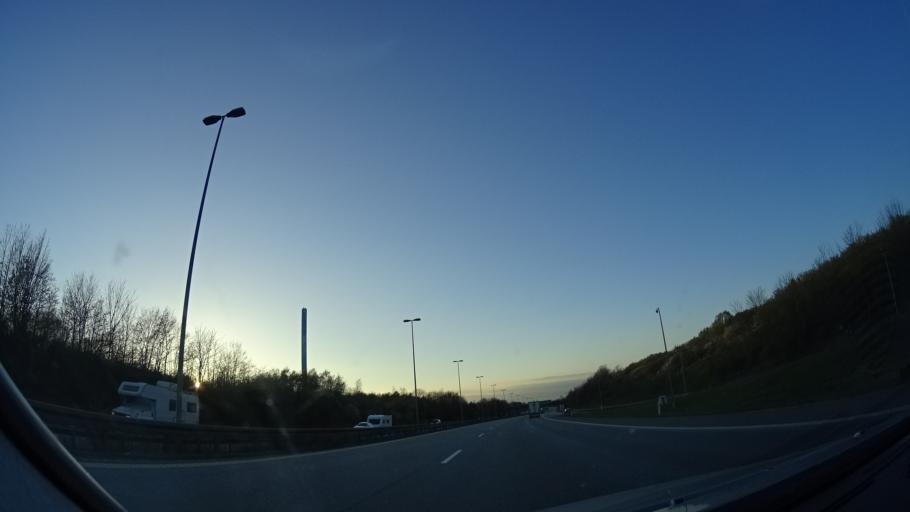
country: DK
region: Capital Region
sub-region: Brondby Kommune
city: Brondbyvester
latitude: 55.6190
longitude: 12.4445
